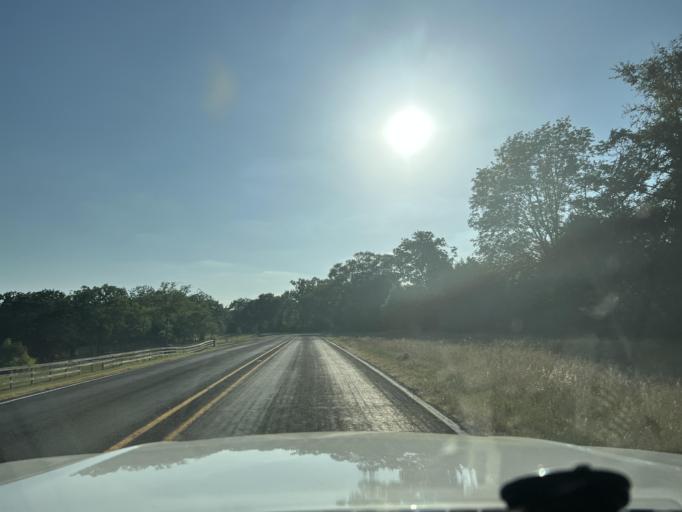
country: US
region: Texas
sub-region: Washington County
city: Brenham
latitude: 30.2343
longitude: -96.2759
